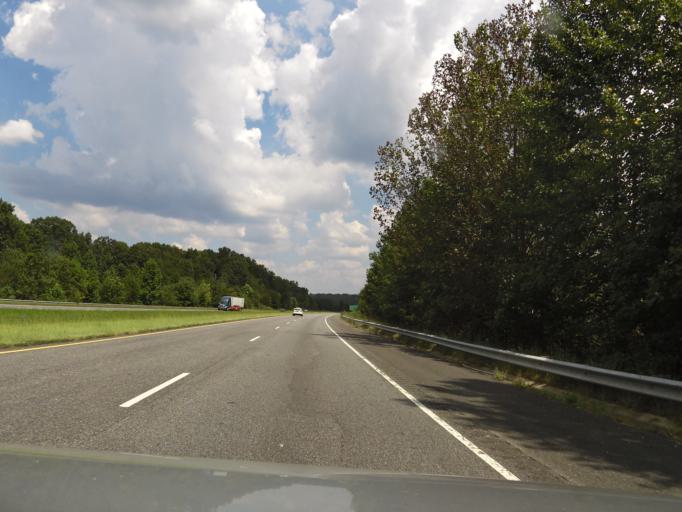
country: US
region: North Carolina
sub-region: Polk County
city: Columbus
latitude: 35.2879
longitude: -82.1014
